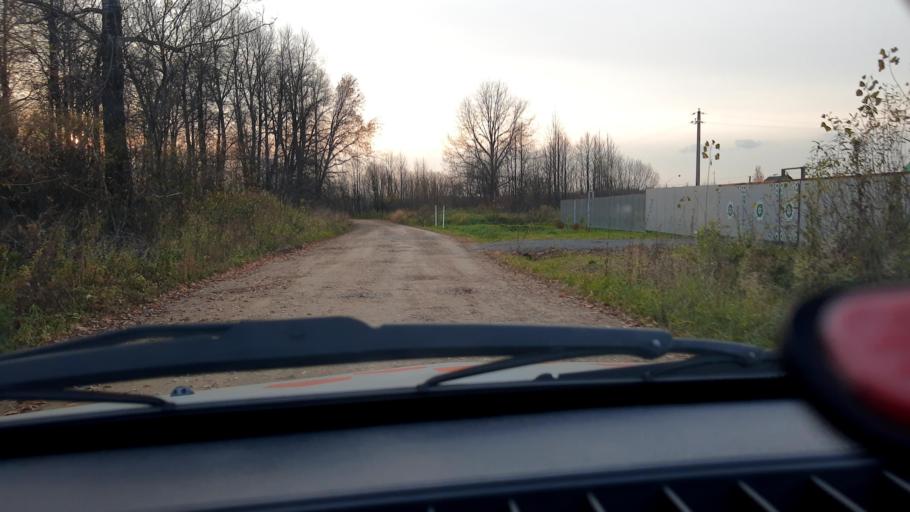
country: RU
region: Bashkortostan
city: Iglino
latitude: 54.7985
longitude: 56.3423
